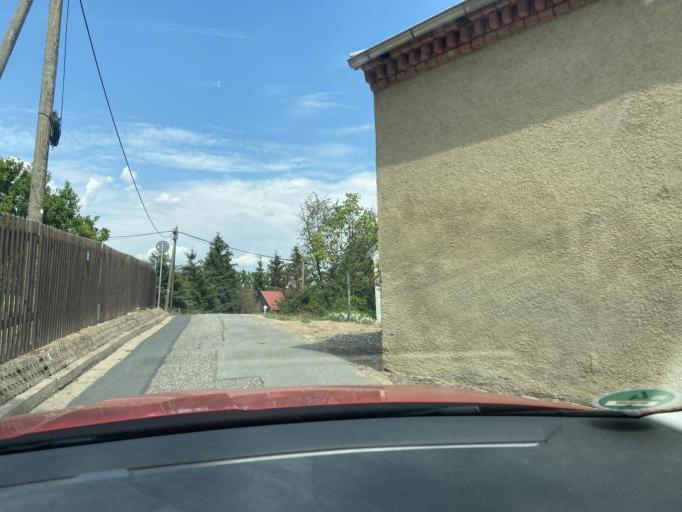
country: DE
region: Saxony
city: Tharandt
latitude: 51.0217
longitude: 13.5931
